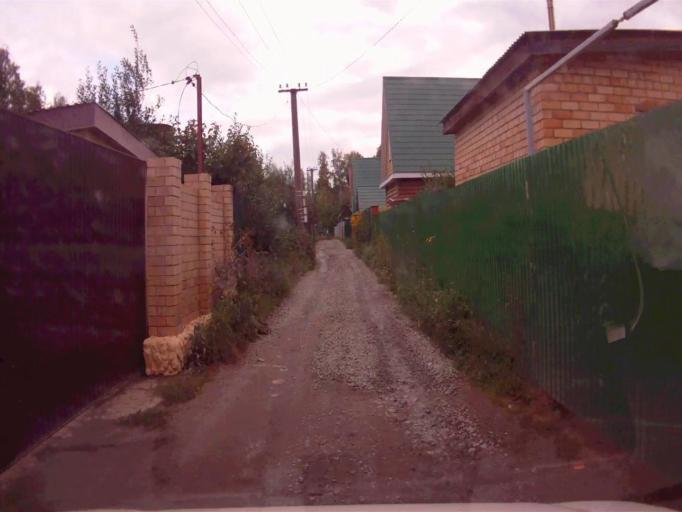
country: RU
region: Chelyabinsk
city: Sargazy
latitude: 55.1302
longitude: 61.2489
